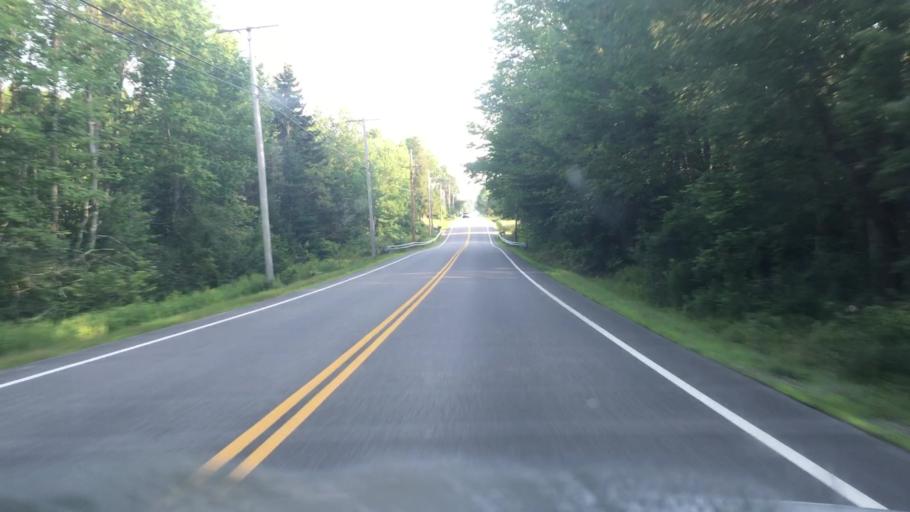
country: US
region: Maine
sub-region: Cumberland County
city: Freeport
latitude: 43.9094
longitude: -70.0917
